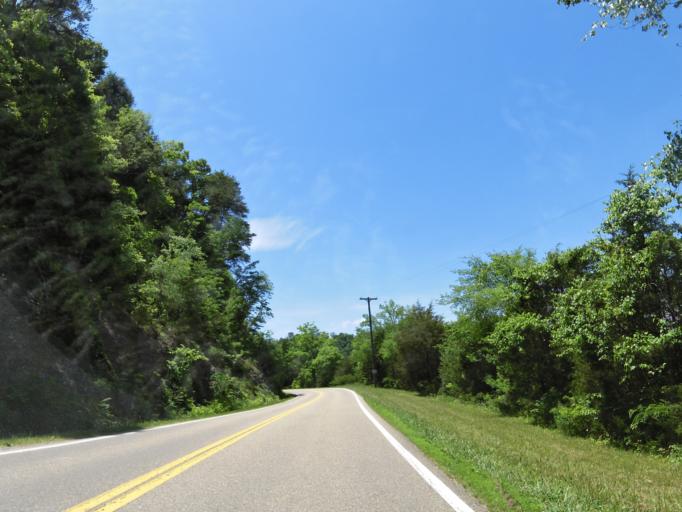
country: US
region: Tennessee
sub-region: Jefferson County
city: Dandridge
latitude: 35.9442
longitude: -83.3683
